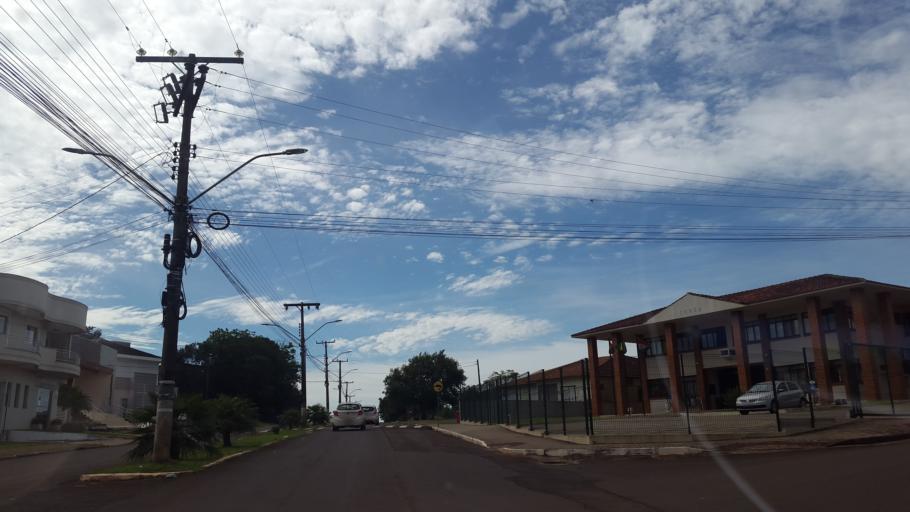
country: AR
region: Misiones
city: Bernardo de Irigoyen
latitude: -26.2611
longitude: -53.6313
